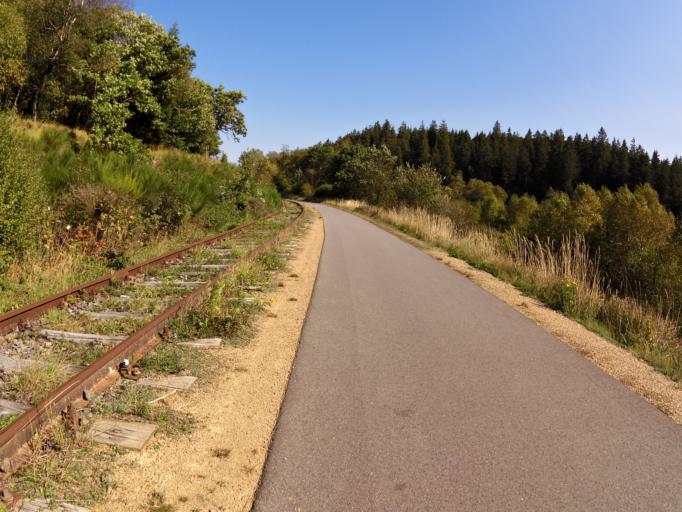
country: BE
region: Wallonia
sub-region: Province de Liege
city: Butgenbach
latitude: 50.4963
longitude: 6.1729
